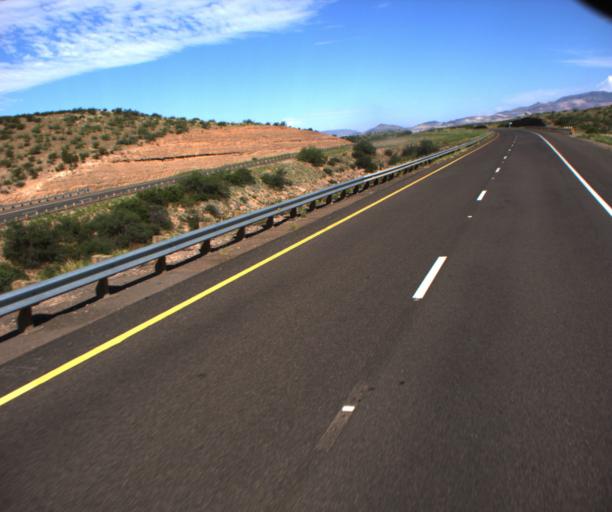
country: US
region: Arizona
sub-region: Greenlee County
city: Clifton
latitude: 32.9751
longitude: -109.2463
